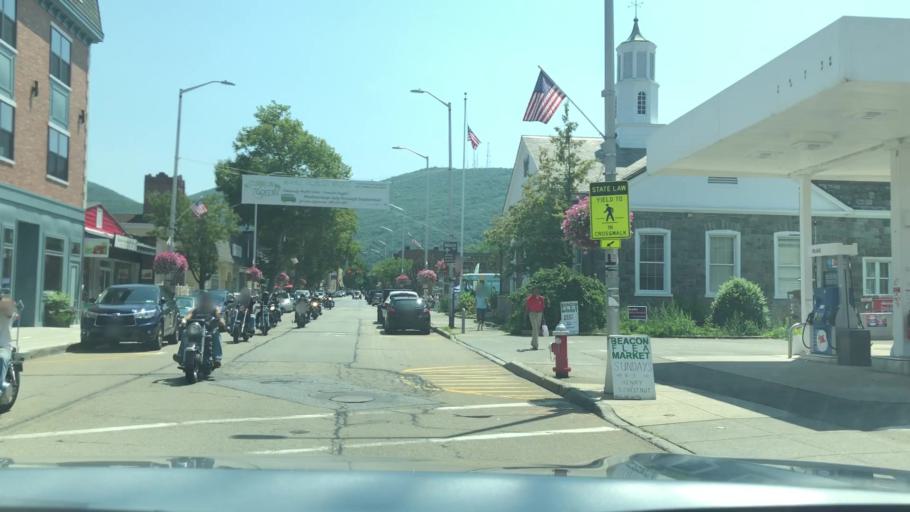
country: US
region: New York
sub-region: Dutchess County
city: Beacon
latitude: 41.5044
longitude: -73.9689
